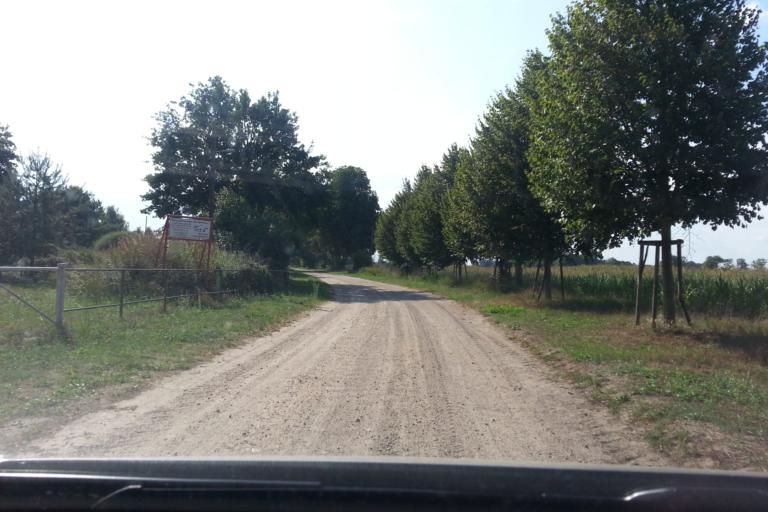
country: DE
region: Mecklenburg-Vorpommern
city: Ferdinandshof
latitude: 53.6423
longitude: 13.8448
